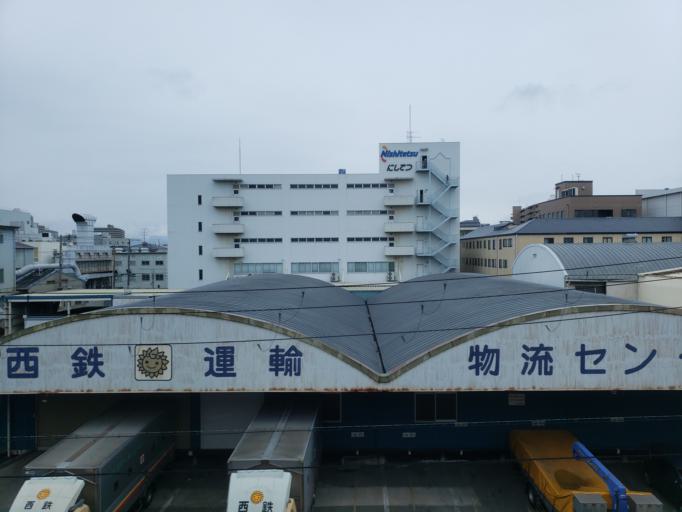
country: JP
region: Hyogo
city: Amagasaki
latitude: 34.7086
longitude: 135.4494
